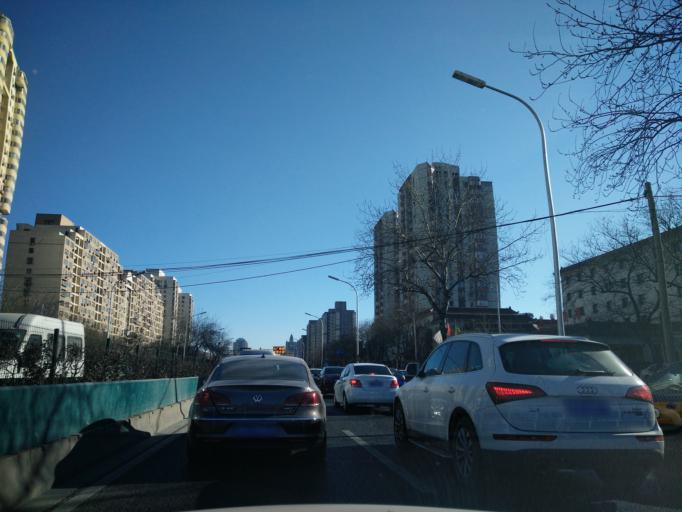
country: CN
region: Beijing
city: Dahongmen
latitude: 39.8557
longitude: 116.3836
